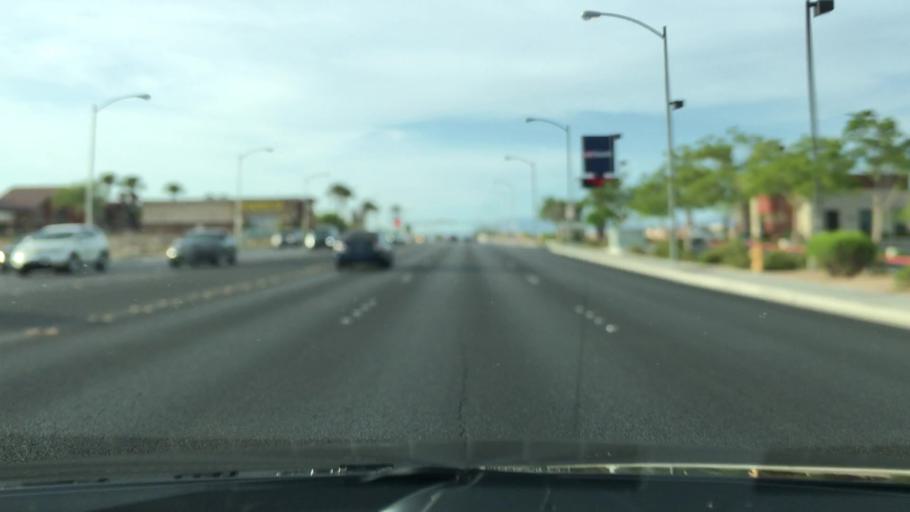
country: US
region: Nevada
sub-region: Clark County
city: Summerlin South
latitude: 36.1044
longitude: -115.2972
